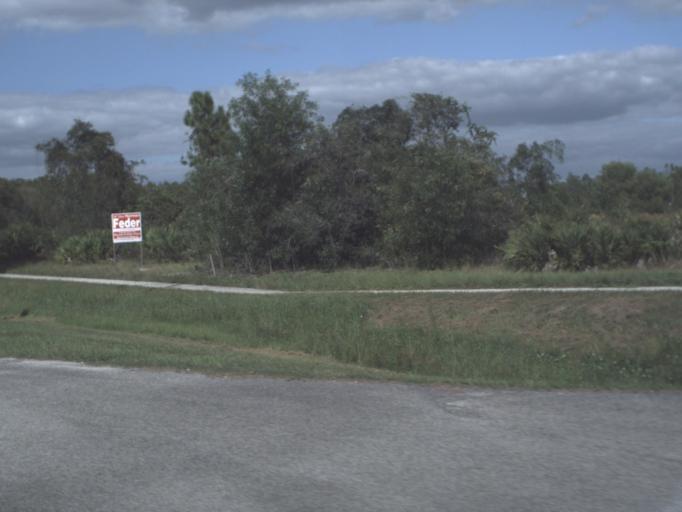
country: US
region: Florida
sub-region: Lee County
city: Bonita Springs
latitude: 26.3062
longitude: -81.8044
